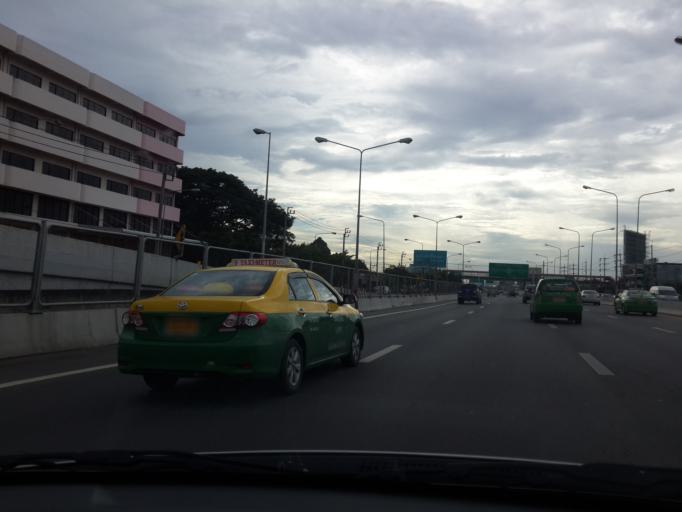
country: TH
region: Bangkok
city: Suan Luang
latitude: 13.7382
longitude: 100.6560
